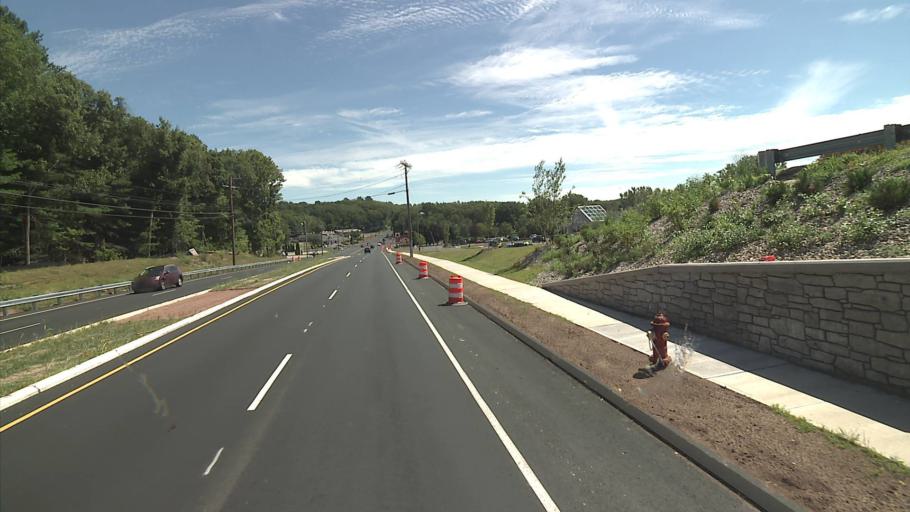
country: US
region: Connecticut
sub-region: Tolland County
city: Tolland
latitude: 41.8608
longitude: -72.3557
